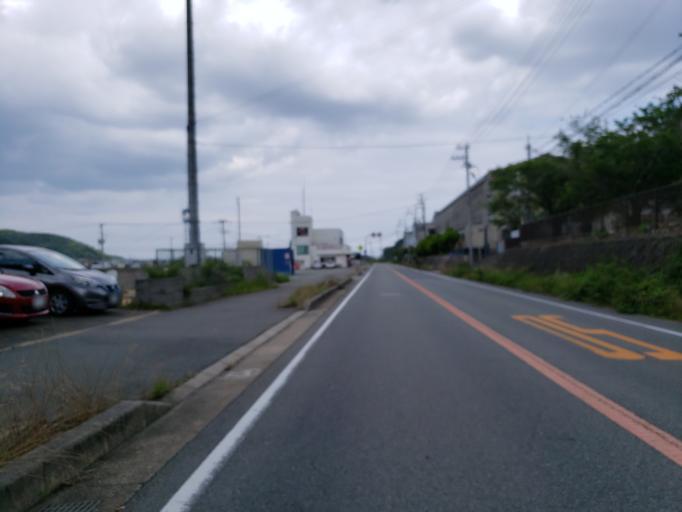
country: JP
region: Hyogo
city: Aioi
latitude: 34.7817
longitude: 134.5382
